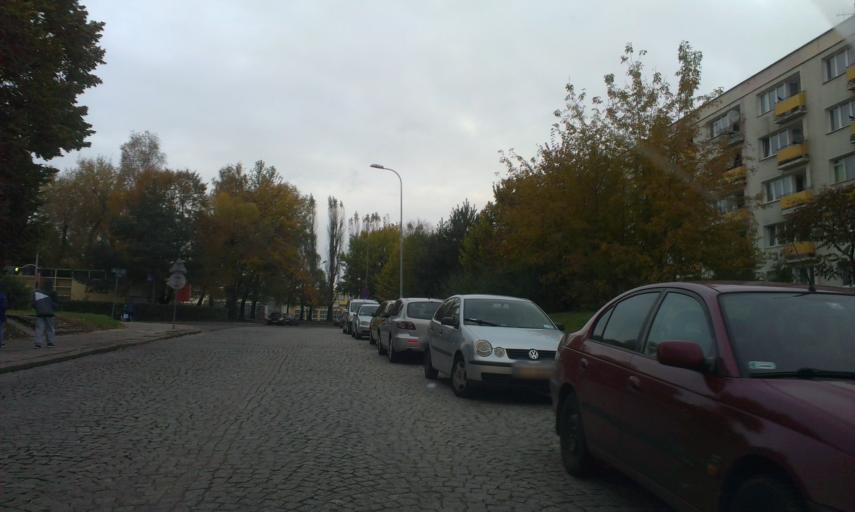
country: PL
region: West Pomeranian Voivodeship
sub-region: Koszalin
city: Koszalin
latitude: 54.2003
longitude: 16.1806
